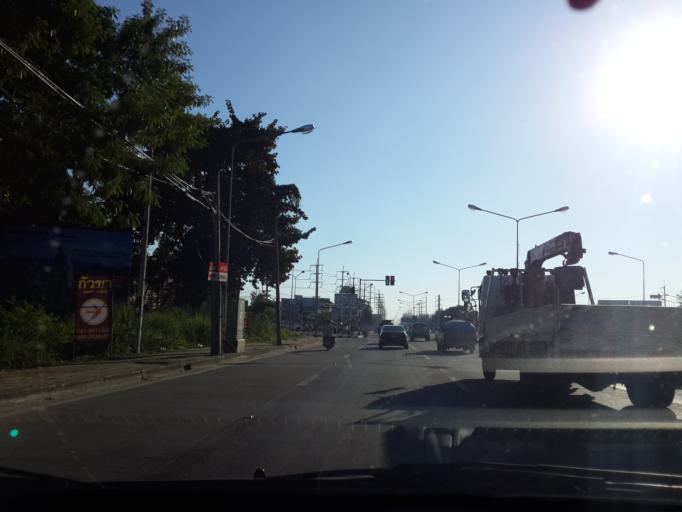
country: TH
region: Chiang Mai
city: Hang Dong
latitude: 18.7236
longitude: 98.9462
